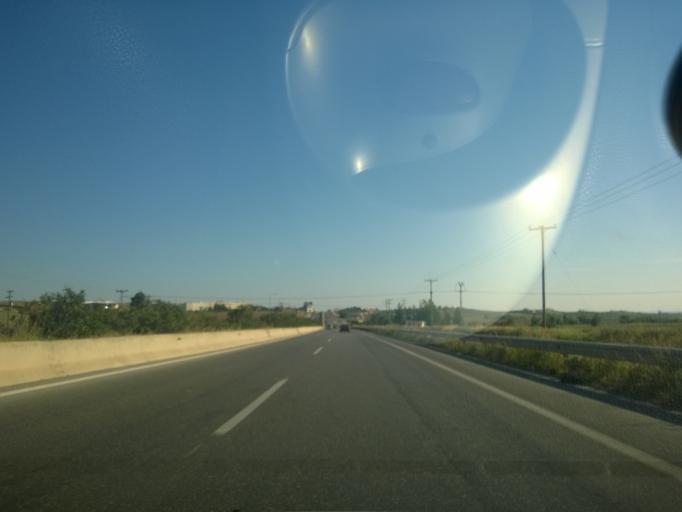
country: GR
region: Central Macedonia
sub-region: Nomos Chalkidikis
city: Lakkoma
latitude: 40.3627
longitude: 23.0499
